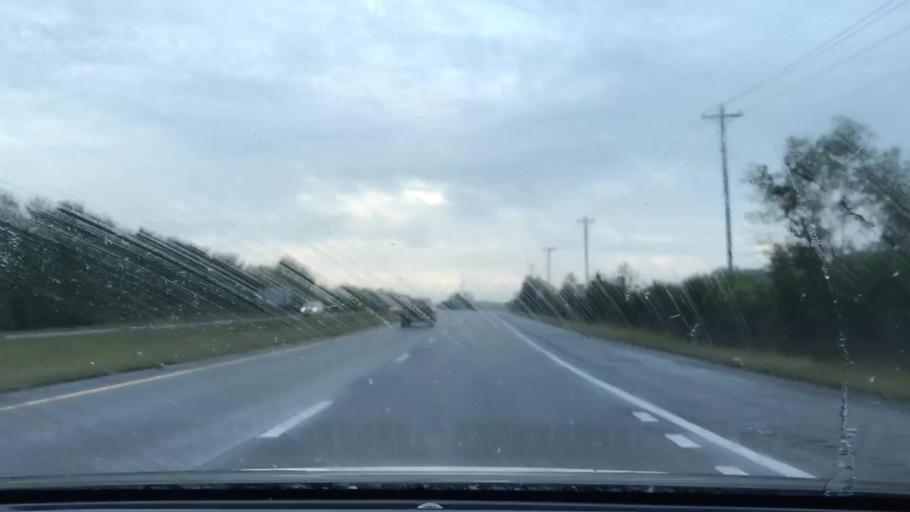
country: US
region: Tennessee
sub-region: Sumner County
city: Gallatin
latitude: 36.3918
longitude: -86.4779
